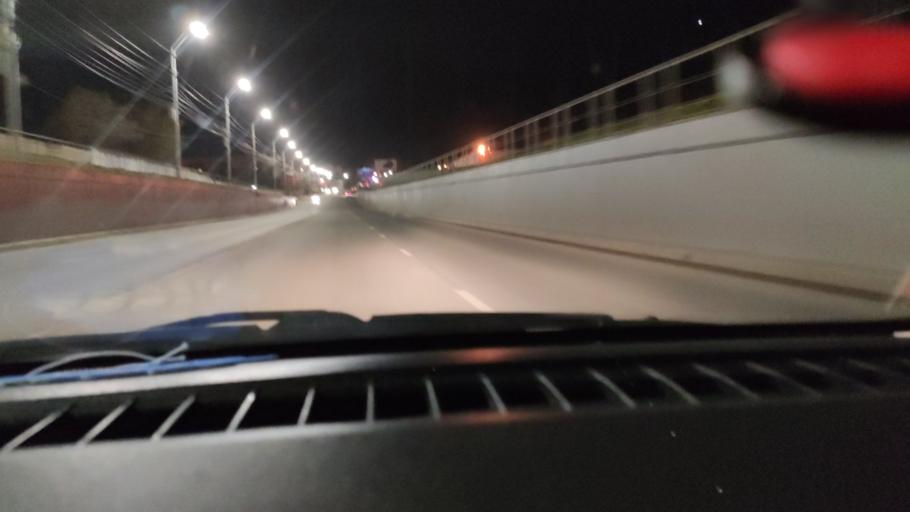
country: RU
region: Saratov
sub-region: Saratovskiy Rayon
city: Saratov
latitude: 51.5577
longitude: 46.0588
